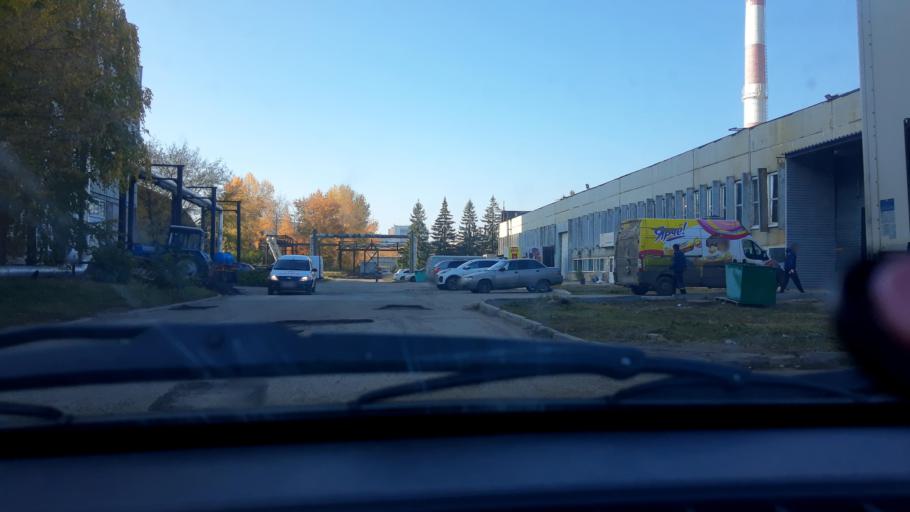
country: RU
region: Bashkortostan
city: Ufa
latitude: 54.7155
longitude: 56.0106
